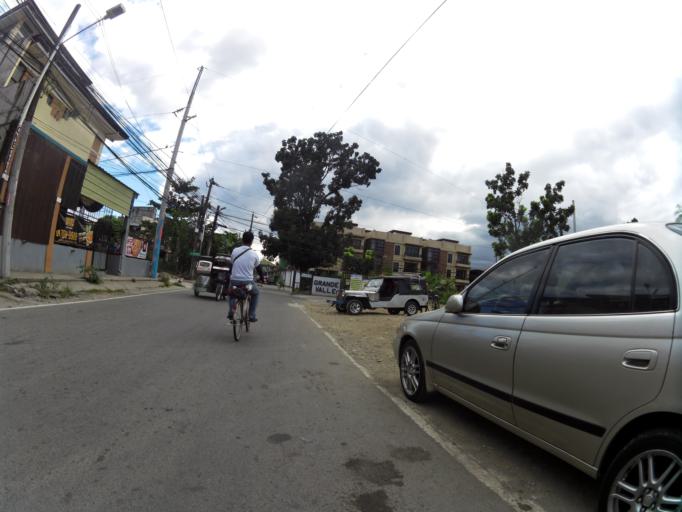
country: PH
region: Calabarzon
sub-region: Province of Rizal
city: Antipolo
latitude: 14.6281
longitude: 121.1079
